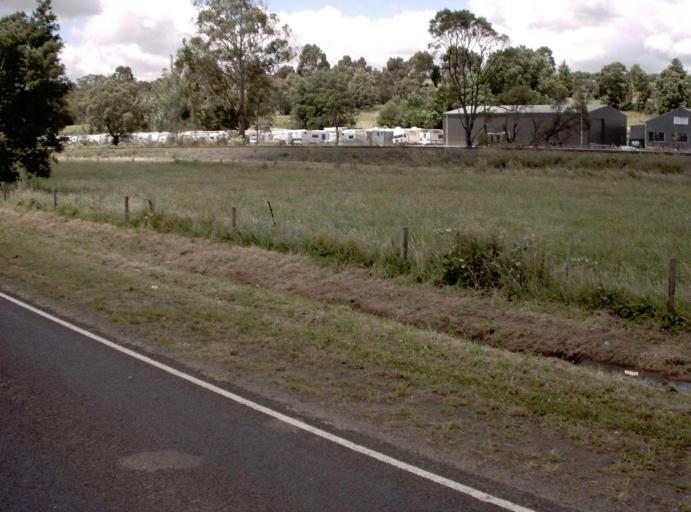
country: AU
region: Victoria
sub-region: Baw Baw
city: Warragul
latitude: -38.1672
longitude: 145.9486
